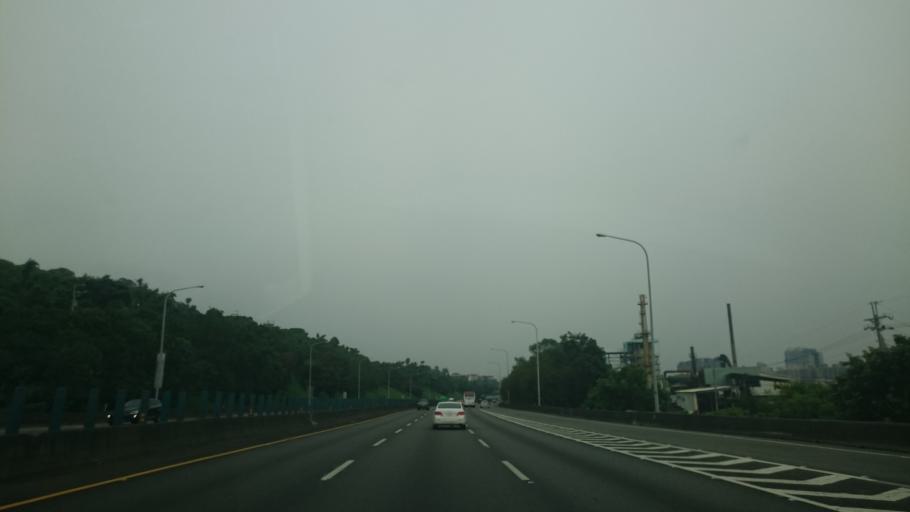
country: TW
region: Taiwan
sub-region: Changhua
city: Chang-hua
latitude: 24.1179
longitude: 120.5879
